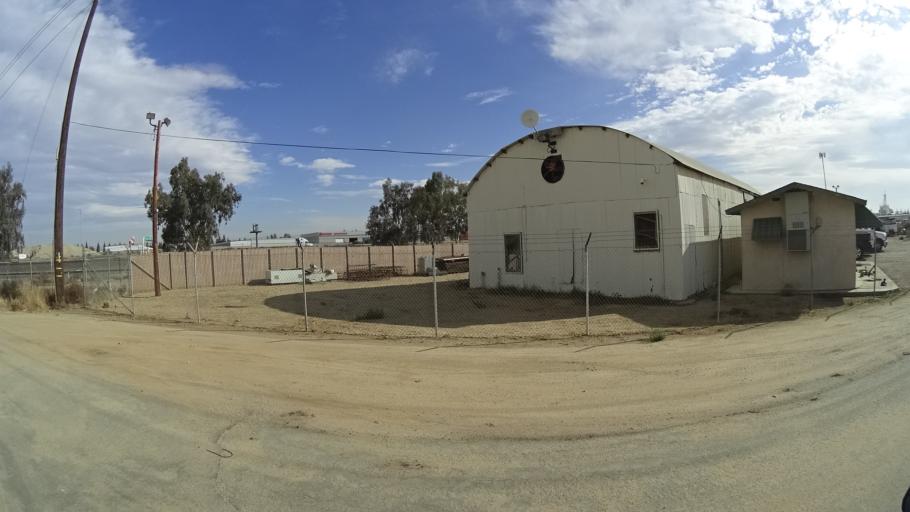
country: US
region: California
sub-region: Kern County
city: Oildale
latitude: 35.4308
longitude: -119.0746
